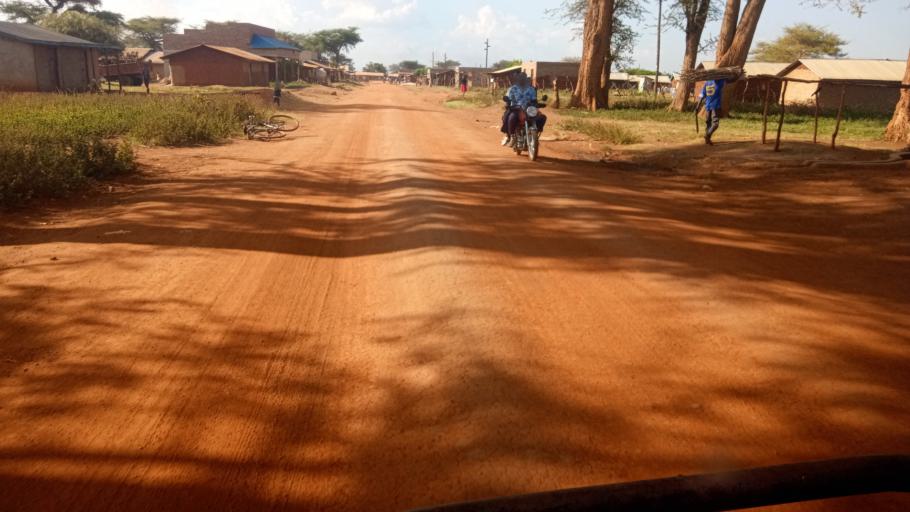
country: UG
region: Eastern Region
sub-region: Kween District
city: Binyin
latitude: 1.5234
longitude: 34.4907
